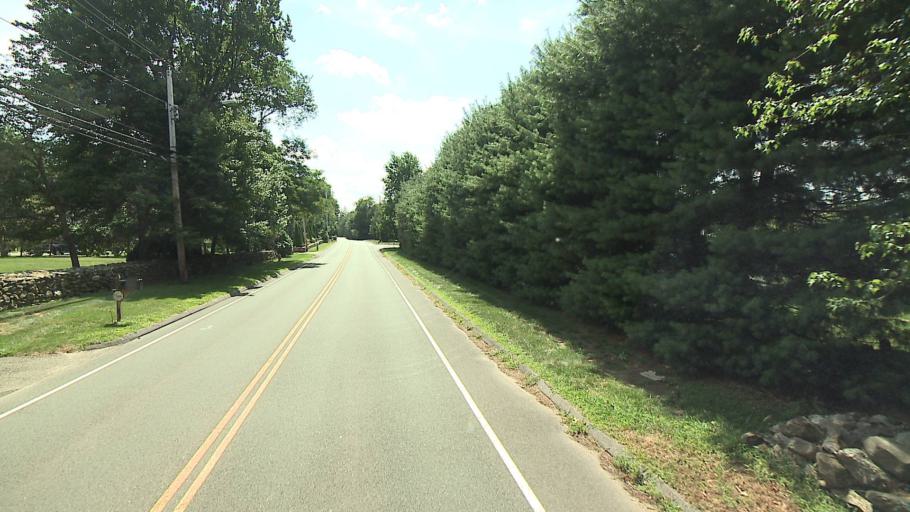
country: US
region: Connecticut
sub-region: Fairfield County
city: Trumbull
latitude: 41.2675
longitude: -73.1656
